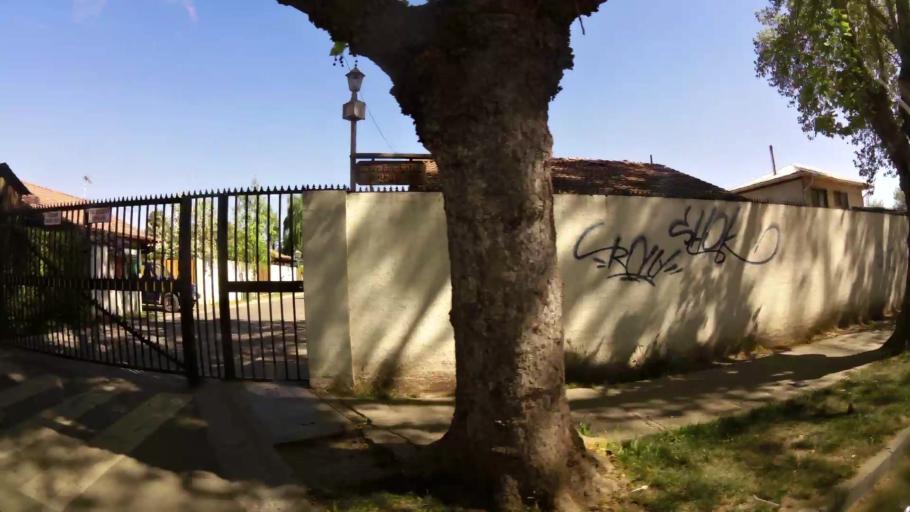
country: CL
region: Santiago Metropolitan
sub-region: Provincia de Talagante
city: Penaflor
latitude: -33.5975
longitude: -70.8799
